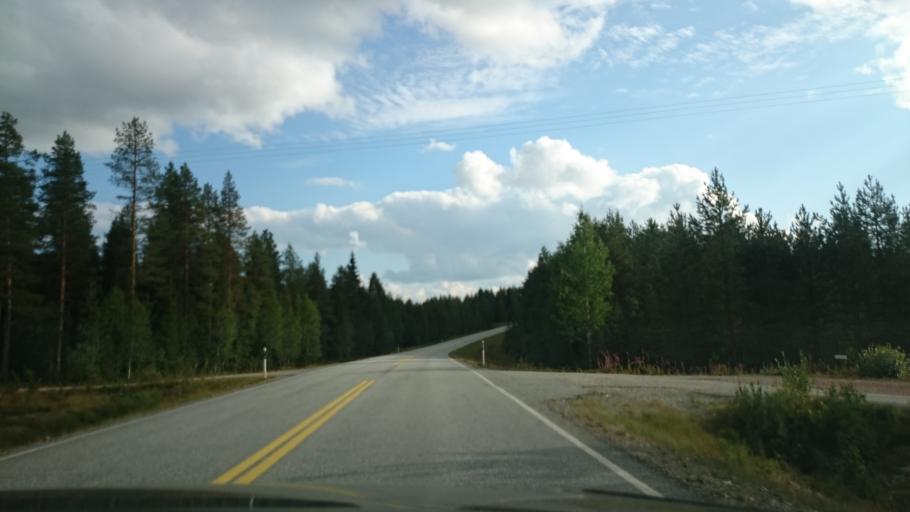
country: FI
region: Kainuu
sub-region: Kehys-Kainuu
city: Kuhmo
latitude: 64.5208
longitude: 29.9463
